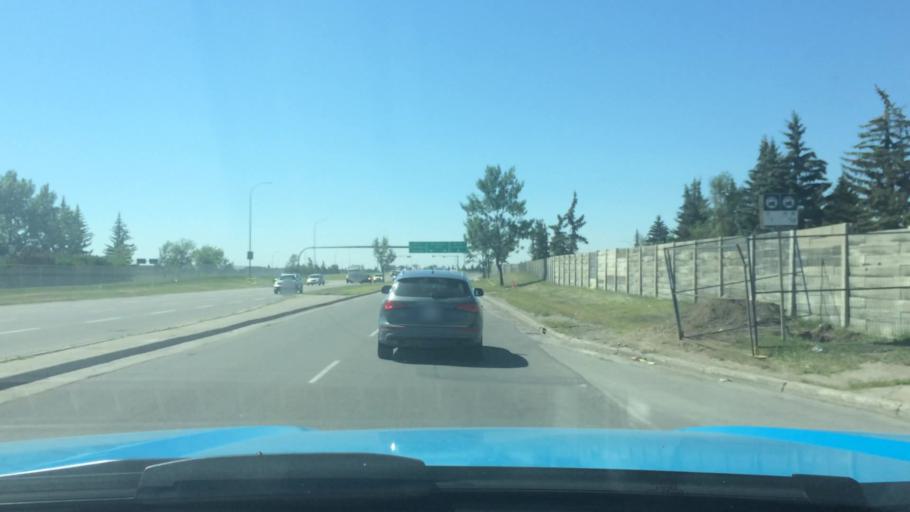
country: CA
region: Alberta
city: Calgary
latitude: 51.0709
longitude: -113.9585
